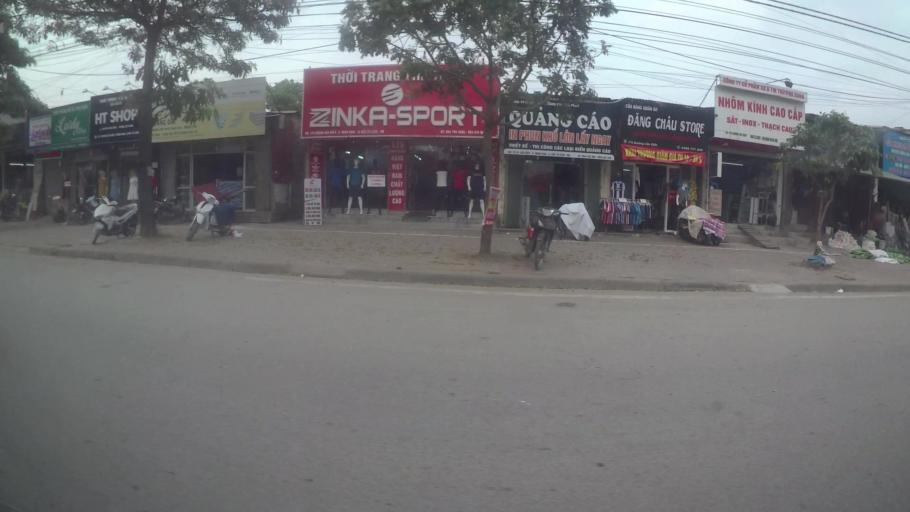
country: VN
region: Ha Noi
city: Cau Dien
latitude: 21.0502
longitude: 105.7397
